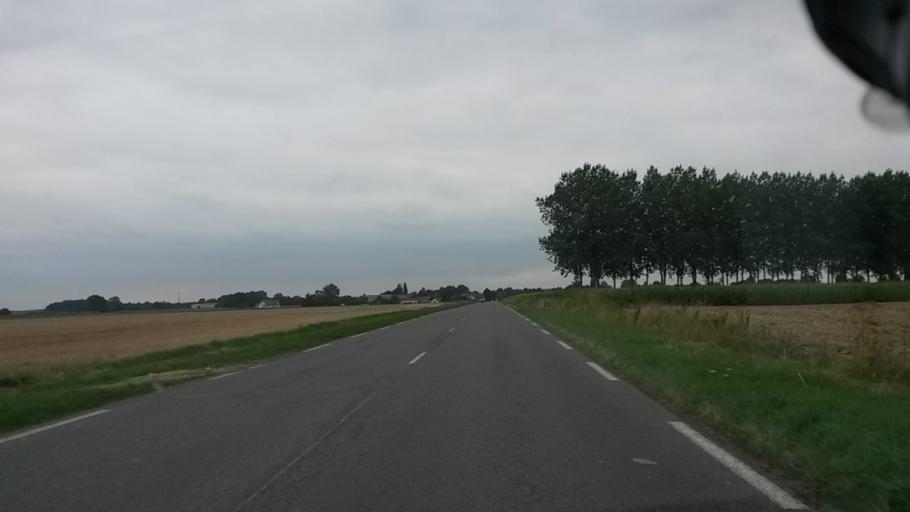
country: FR
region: Picardie
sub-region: Departement de la Somme
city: Hornoy-le-Bourg
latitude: 49.7811
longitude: 1.9042
